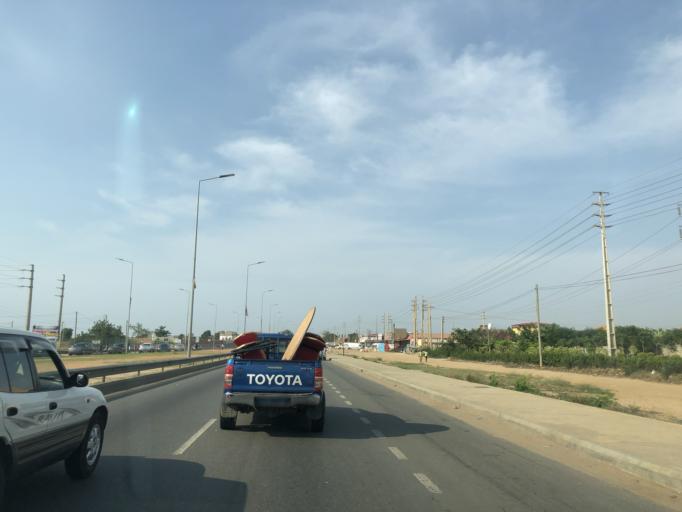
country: AO
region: Luanda
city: Luanda
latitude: -8.9423
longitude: 13.2612
